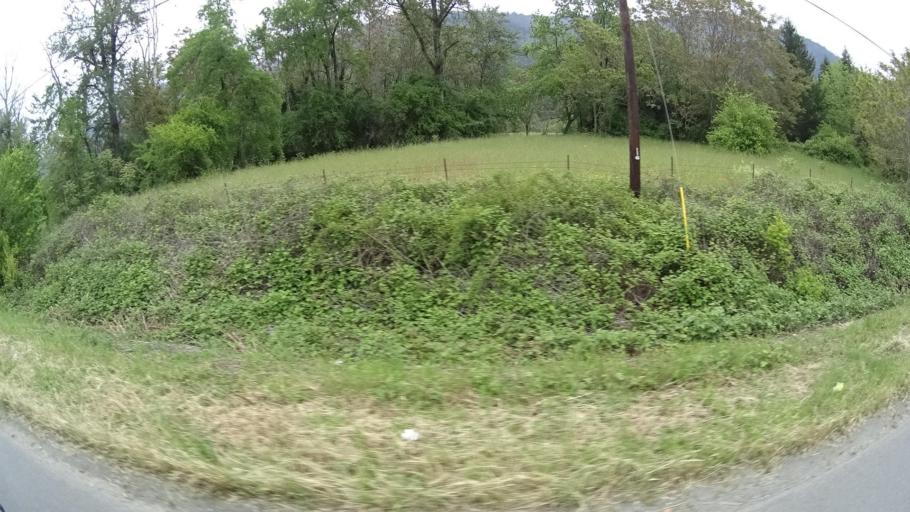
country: US
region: California
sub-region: Humboldt County
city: Willow Creek
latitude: 41.0580
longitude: -123.6838
